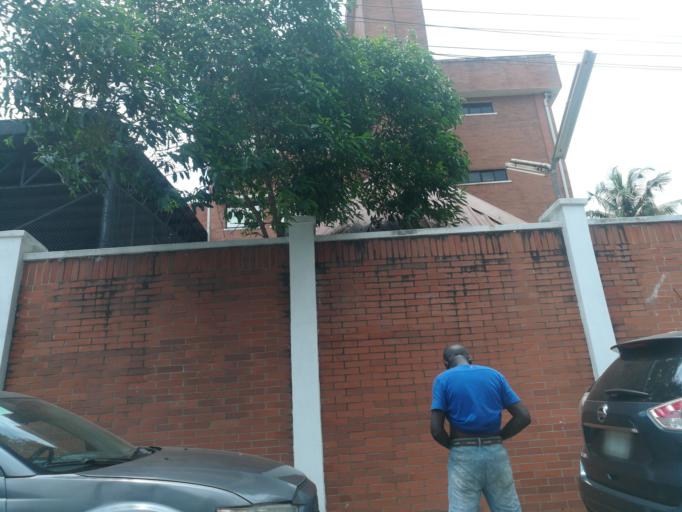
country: NG
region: Lagos
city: Somolu
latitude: 6.5518
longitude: 3.3645
